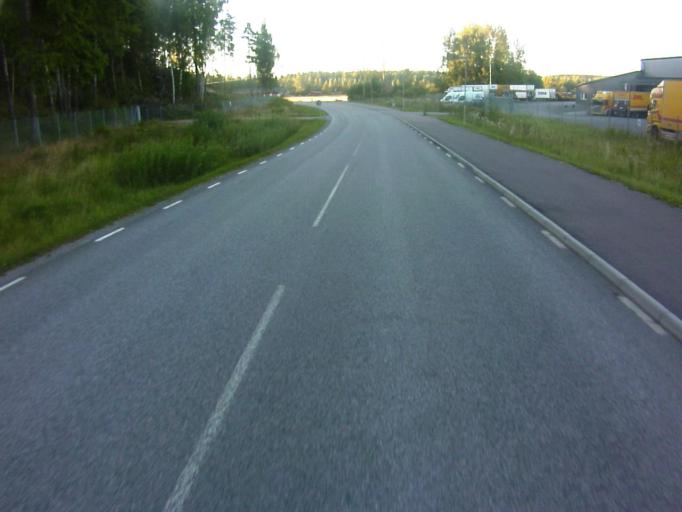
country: SE
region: Soedermanland
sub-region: Eskilstuna Kommun
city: Hallbybrunn
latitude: 59.4048
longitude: 16.4365
